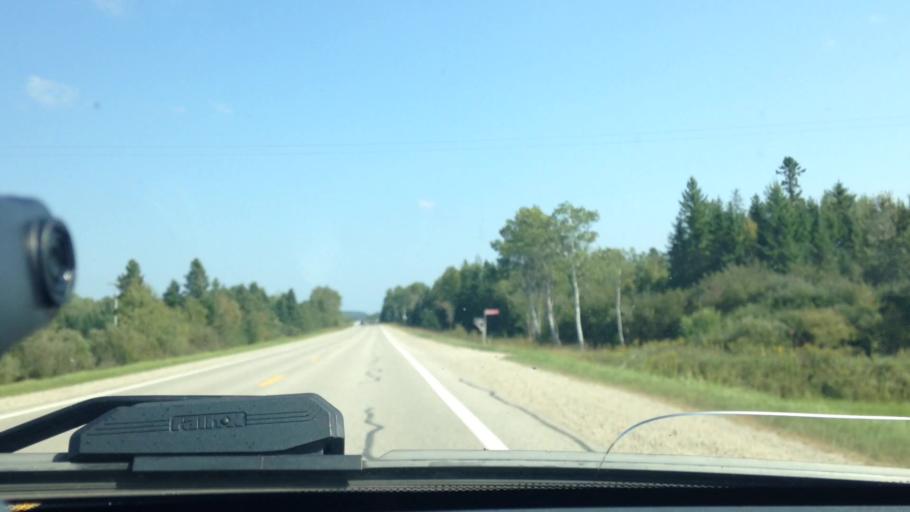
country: US
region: Michigan
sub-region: Luce County
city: Newberry
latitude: 46.3103
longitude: -85.6210
